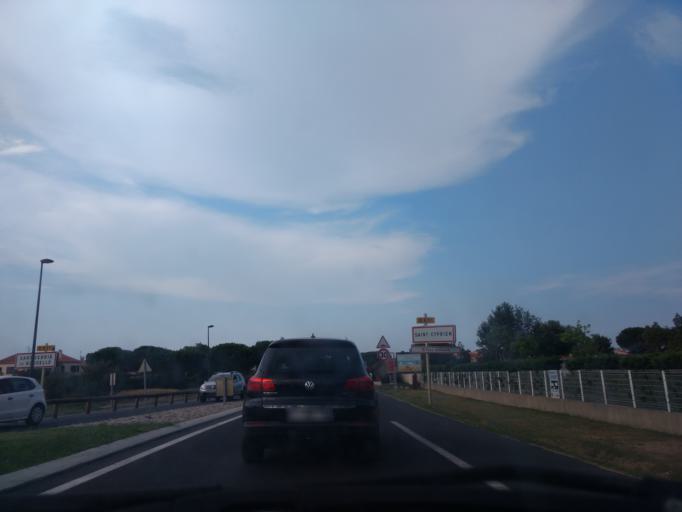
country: FR
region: Languedoc-Roussillon
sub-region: Departement des Pyrenees-Orientales
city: Saint-Cyprien-Plage
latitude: 42.6254
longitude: 3.0234
